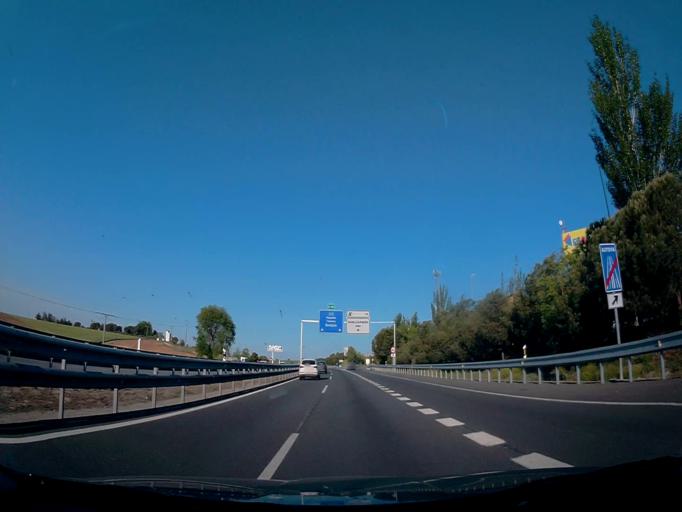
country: ES
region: Madrid
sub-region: Provincia de Madrid
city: Navalcarnero
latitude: 40.2910
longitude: -3.9905
